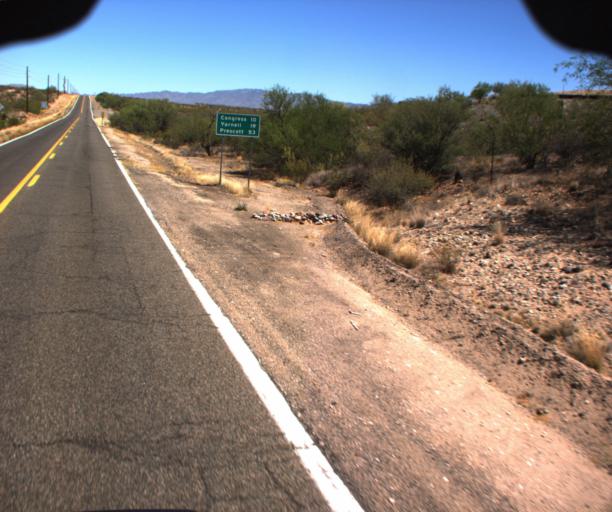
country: US
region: Arizona
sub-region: Maricopa County
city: Wickenburg
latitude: 34.0318
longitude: -112.8117
